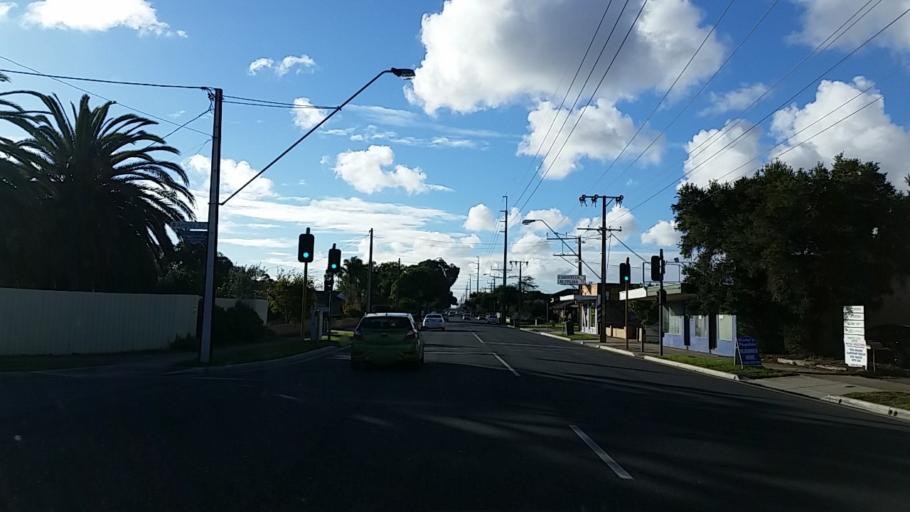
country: AU
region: South Australia
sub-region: Charles Sturt
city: Findon
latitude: -34.9002
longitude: 138.5322
